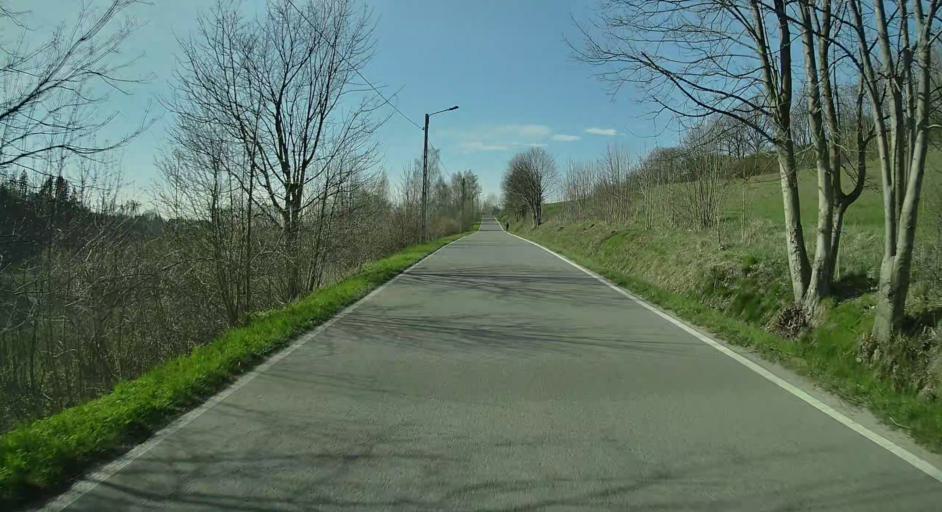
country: PL
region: Lower Silesian Voivodeship
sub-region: Powiat klodzki
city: Lewin Klodzki
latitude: 50.3996
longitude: 16.2958
